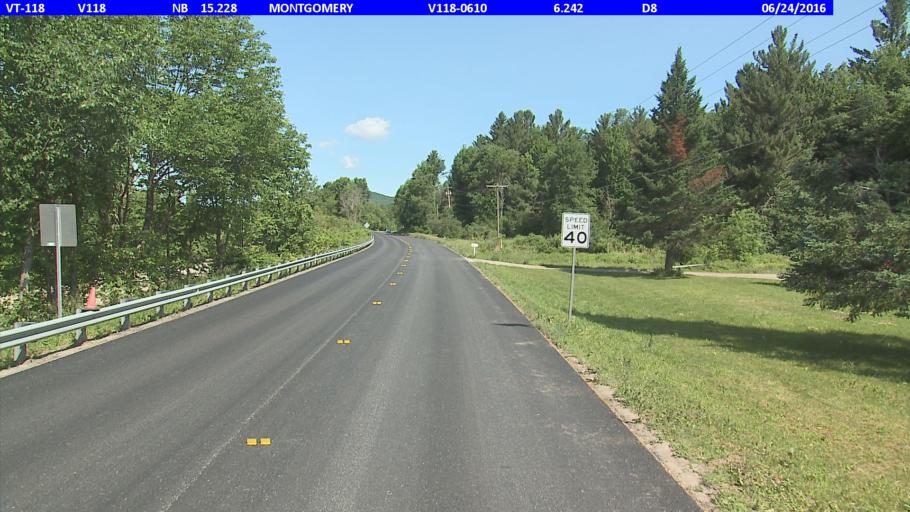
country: US
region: Vermont
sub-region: Franklin County
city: Richford
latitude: 44.8839
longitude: -72.6169
